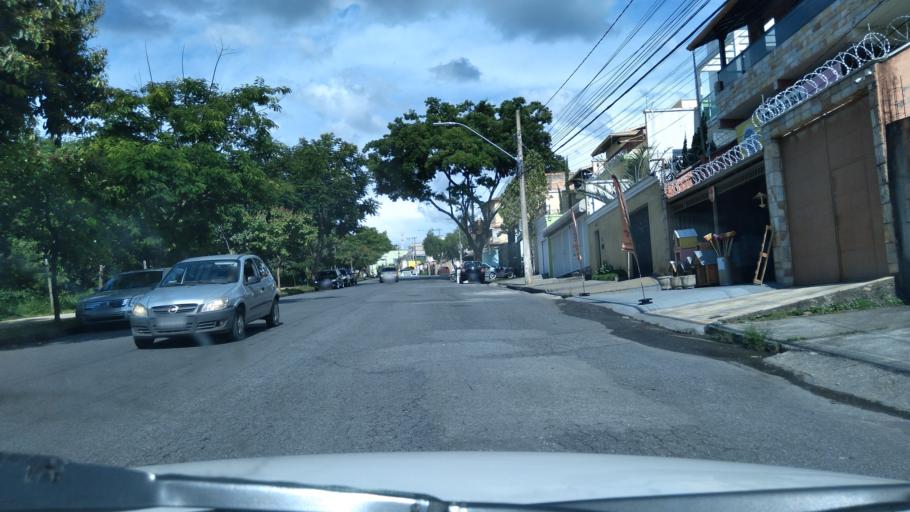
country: BR
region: Minas Gerais
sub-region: Belo Horizonte
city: Belo Horizonte
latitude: -19.8611
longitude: -43.8870
